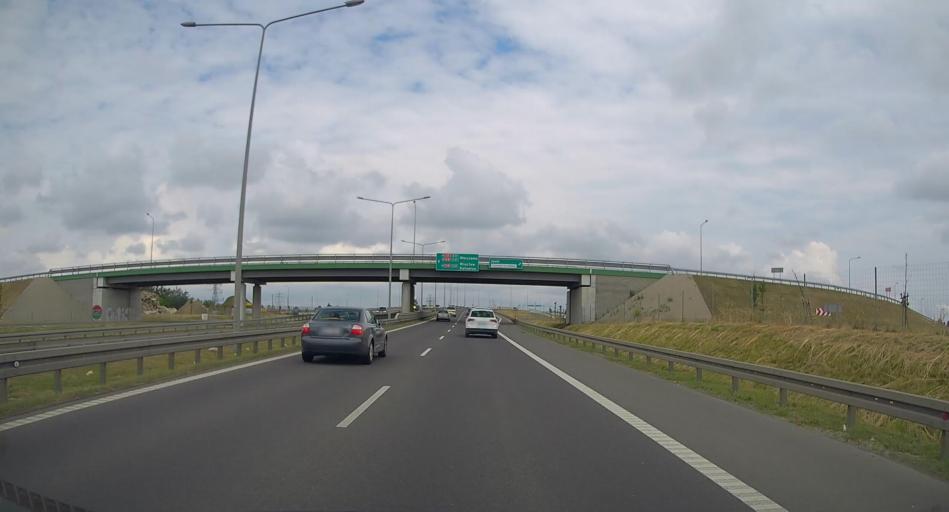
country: PL
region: Masovian Voivodeship
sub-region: Powiat pruszkowski
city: Nowe Grocholice
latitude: 52.1208
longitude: 20.8822
